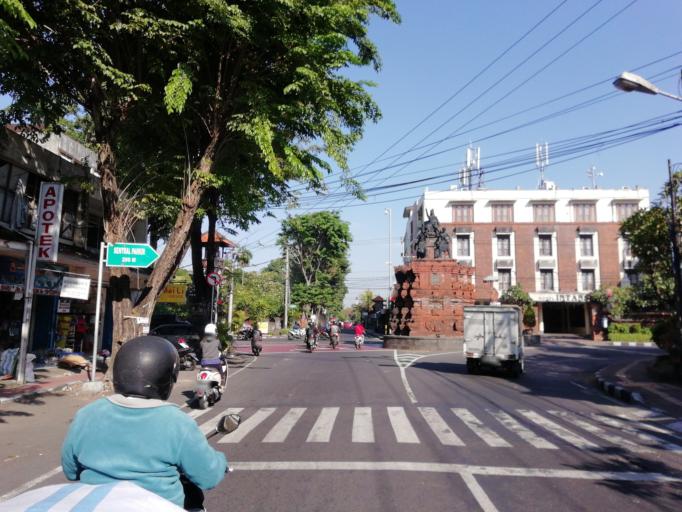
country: ID
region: Bali
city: Denpasar
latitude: -8.6584
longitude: 115.2102
